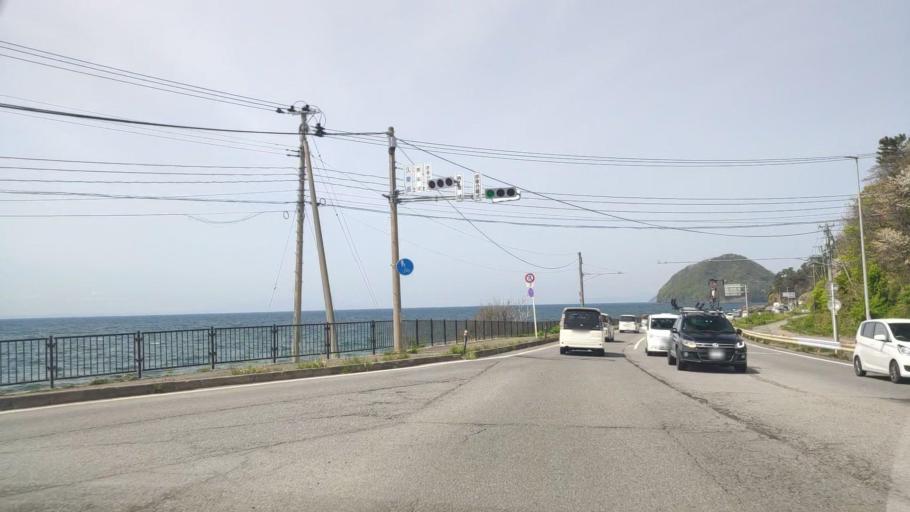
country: JP
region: Aomori
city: Aomori Shi
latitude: 40.8775
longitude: 140.8500
